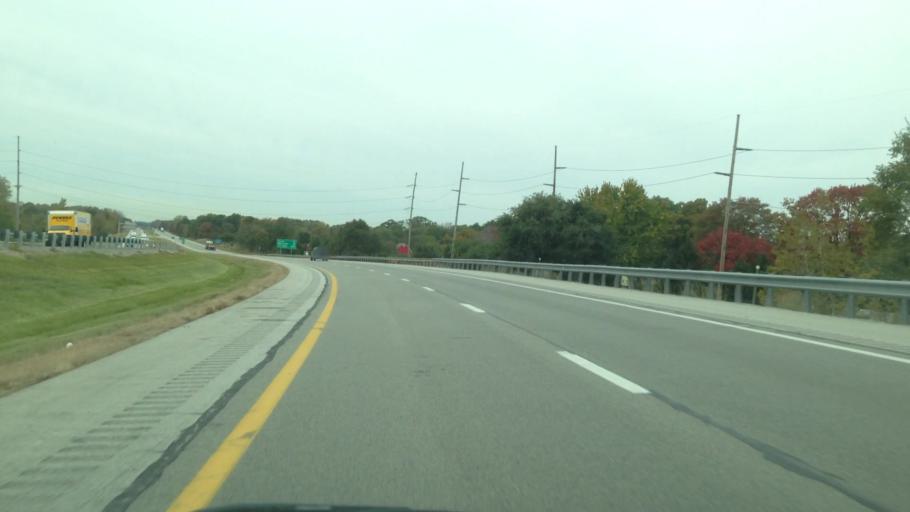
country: US
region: Ohio
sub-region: Fulton County
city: Swanton
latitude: 41.6027
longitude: -83.8104
